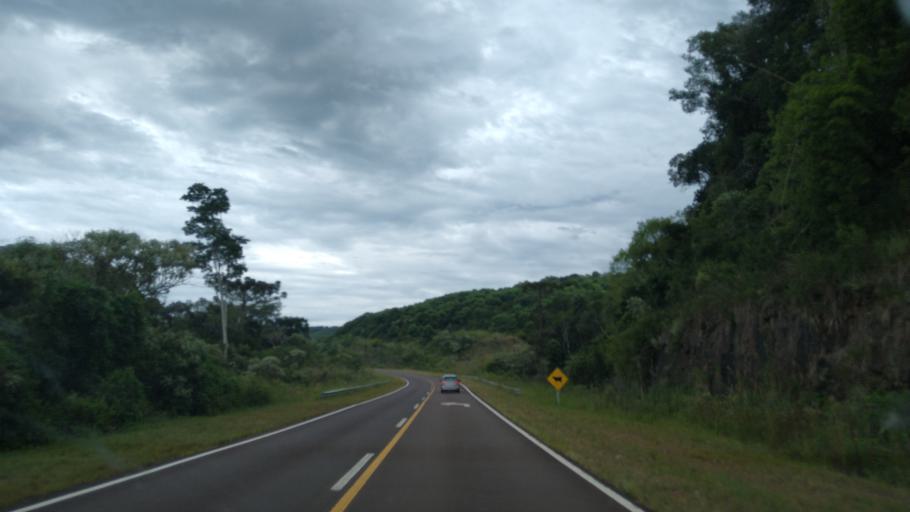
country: AR
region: Misiones
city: Bernardo de Irigoyen
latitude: -26.3311
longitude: -53.7619
